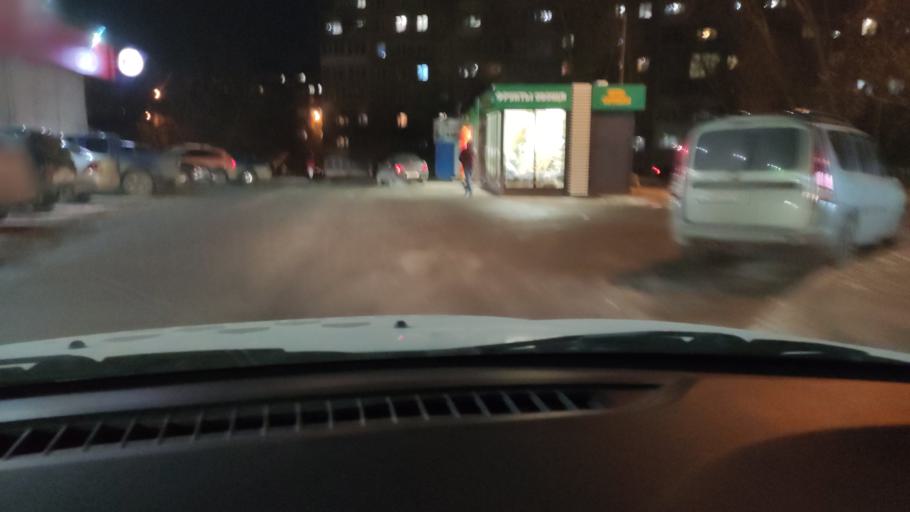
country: RU
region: Perm
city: Perm
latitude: 57.9786
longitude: 56.2326
